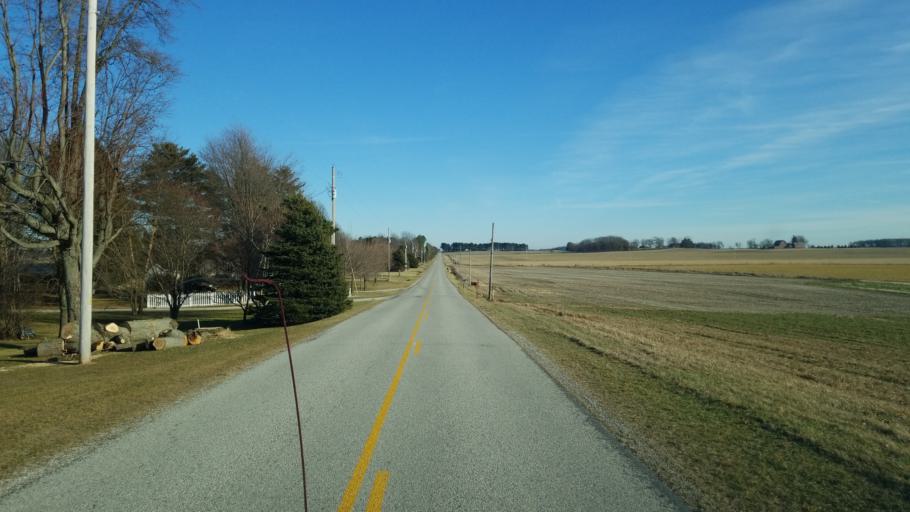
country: US
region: Ohio
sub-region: Sandusky County
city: Green Springs
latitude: 41.2560
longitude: -83.0008
